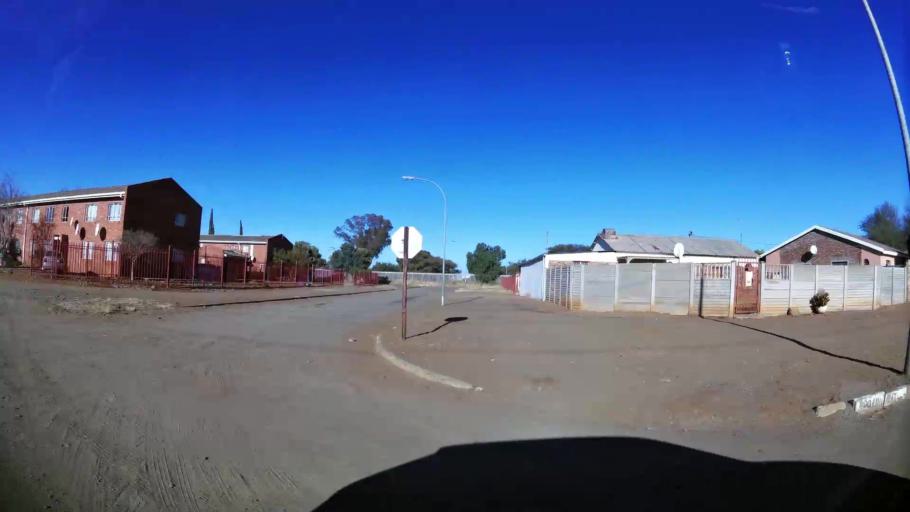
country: ZA
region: Northern Cape
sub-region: Frances Baard District Municipality
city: Kimberley
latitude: -28.7617
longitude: 24.7815
